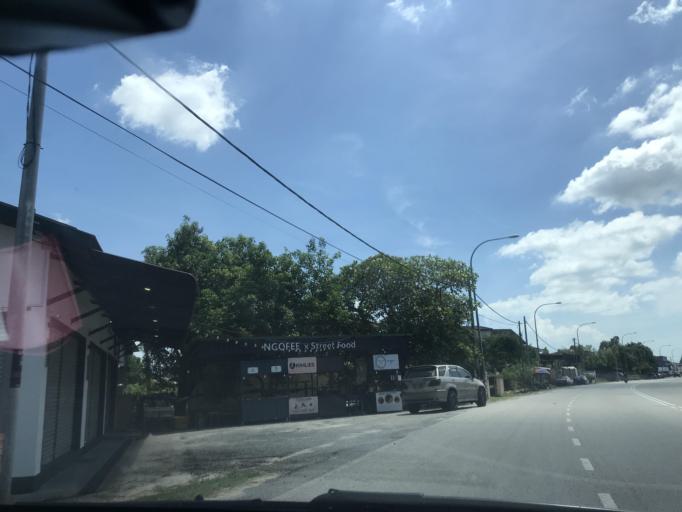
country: MY
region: Kelantan
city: Kota Bharu
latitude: 6.1112
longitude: 102.2636
